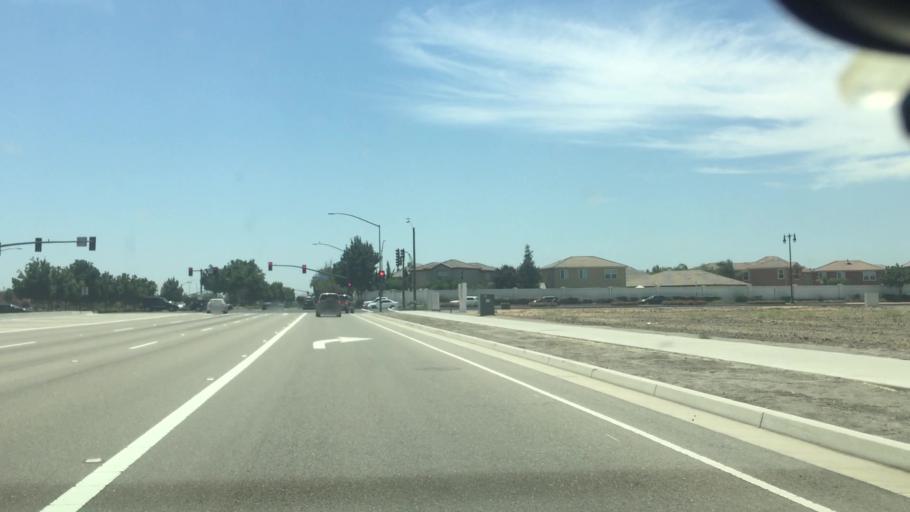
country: US
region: California
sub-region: San Joaquin County
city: Lathrop
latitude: 37.8128
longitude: -121.3004
